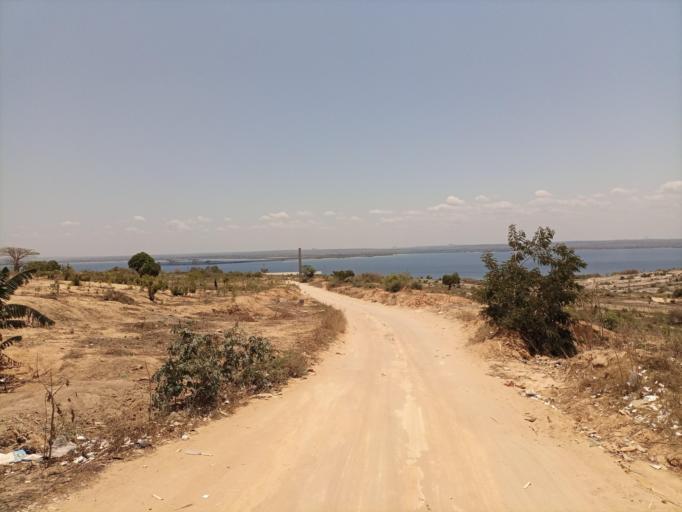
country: MZ
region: Nampula
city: Nacala
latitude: -14.5173
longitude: 40.6838
